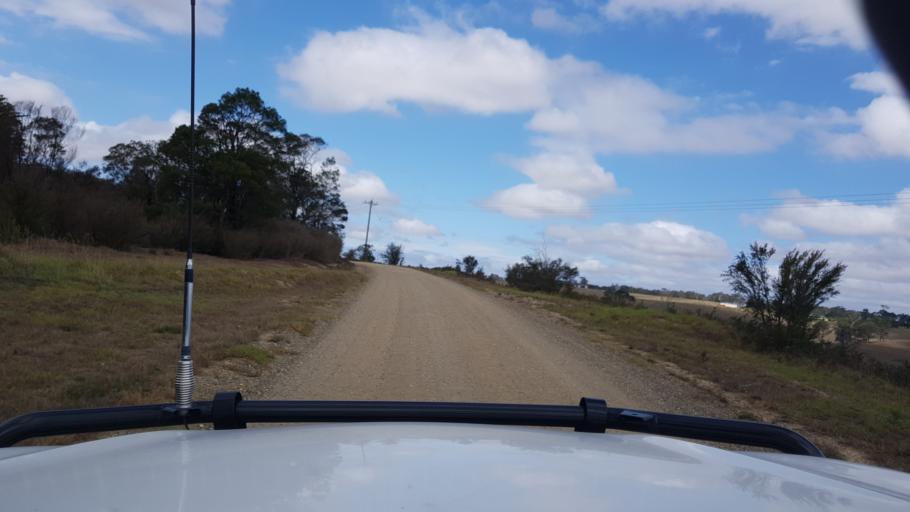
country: AU
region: Victoria
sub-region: East Gippsland
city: Bairnsdale
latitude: -37.7875
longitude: 147.5614
